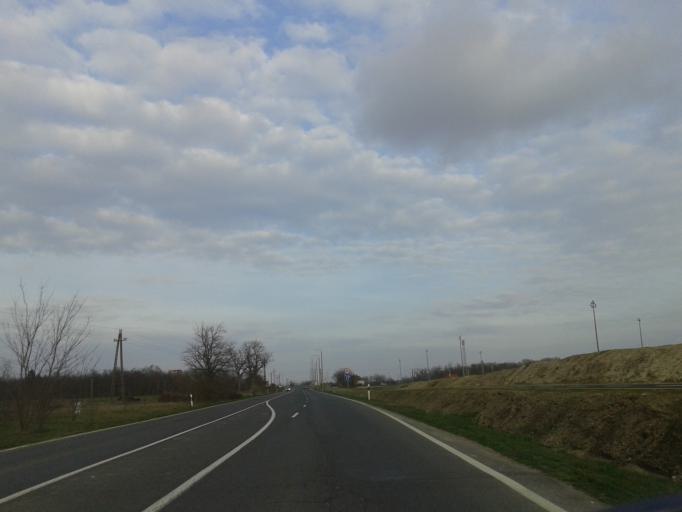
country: HU
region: Gyor-Moson-Sopron
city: Toltestava
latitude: 47.7312
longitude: 17.7627
